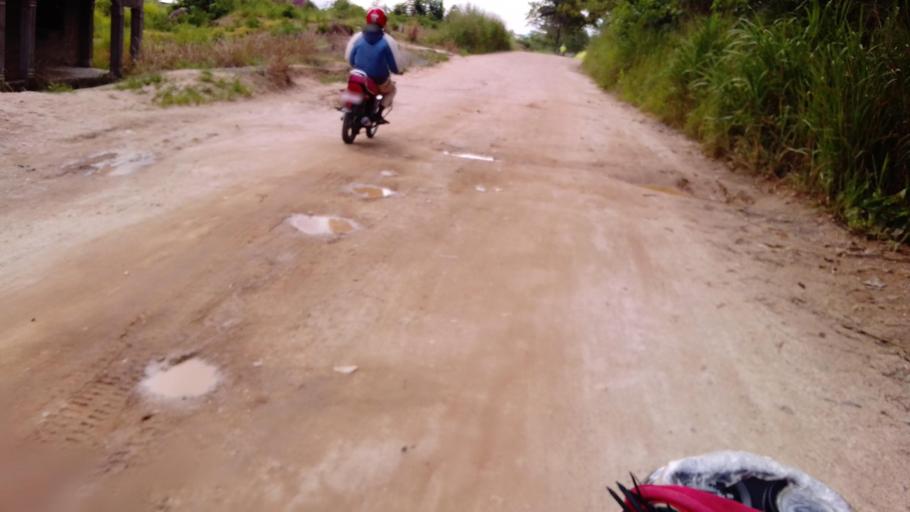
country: SL
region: Eastern Province
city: Koidu
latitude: 8.6680
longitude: -10.9772
